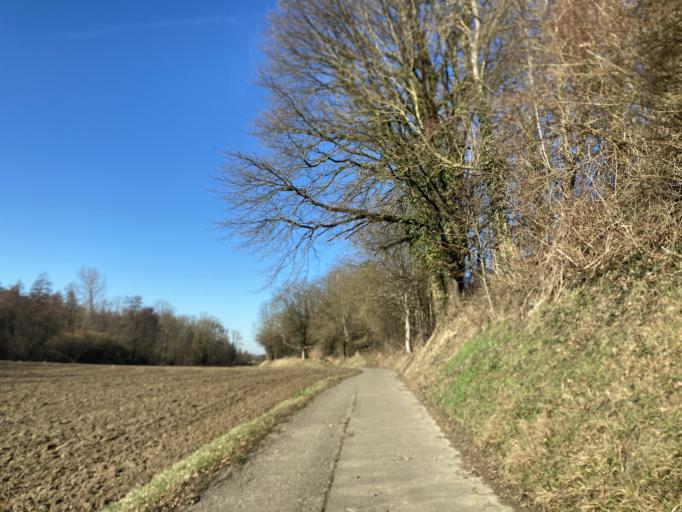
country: DE
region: Baden-Wuerttemberg
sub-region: Freiburg Region
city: Eichstetten
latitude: 48.0823
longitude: 7.7723
